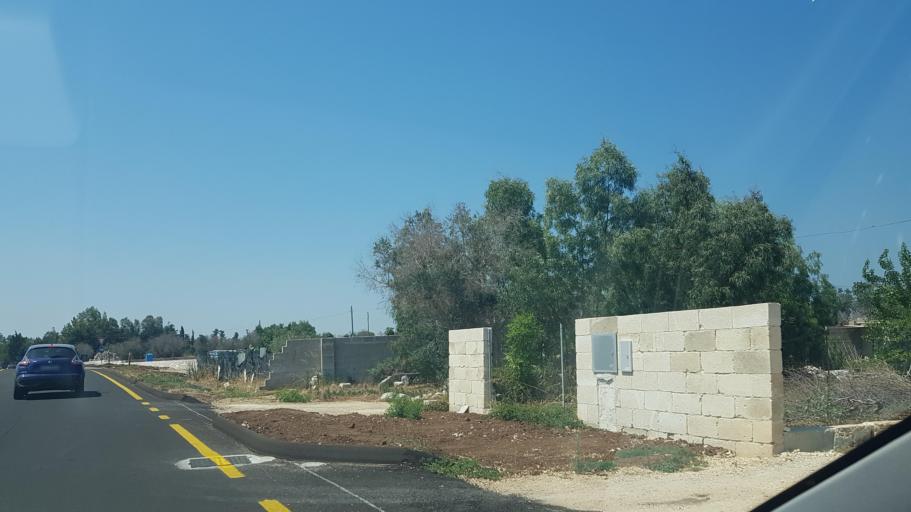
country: IT
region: Apulia
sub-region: Provincia di Lecce
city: Merine
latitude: 40.3309
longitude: 18.2473
